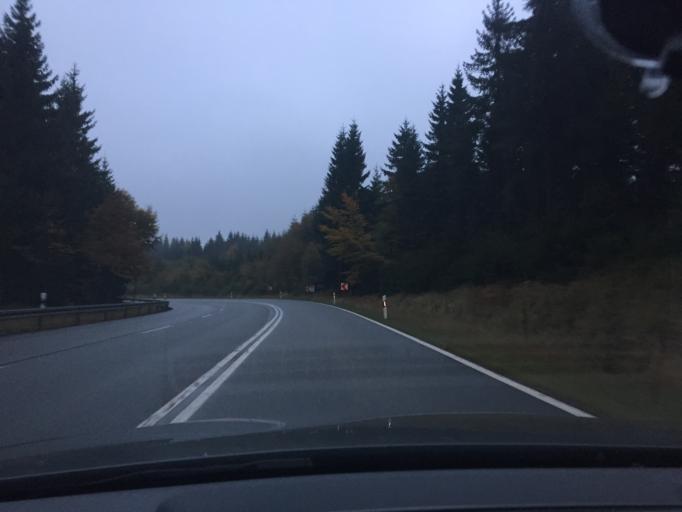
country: DE
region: Saxony
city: Altenberg
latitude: 50.7697
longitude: 13.7266
